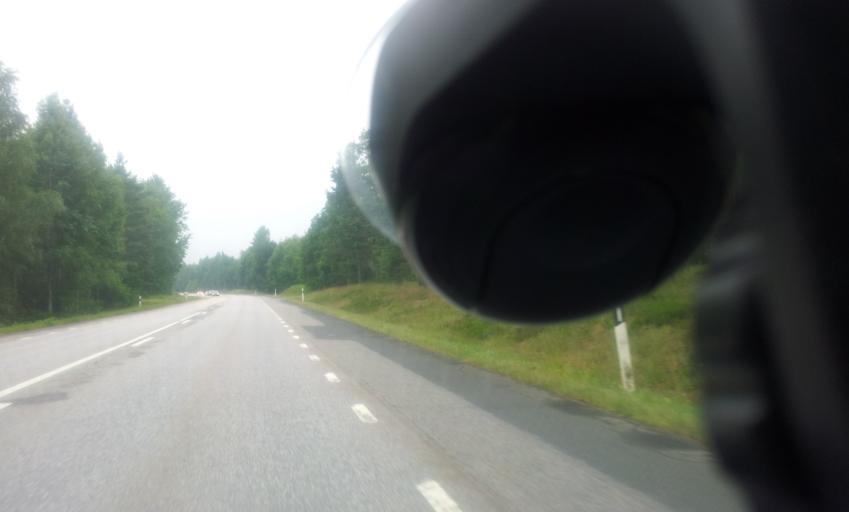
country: SE
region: Kalmar
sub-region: Vasterviks Kommun
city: Ankarsrum
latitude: 57.6958
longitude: 16.4410
